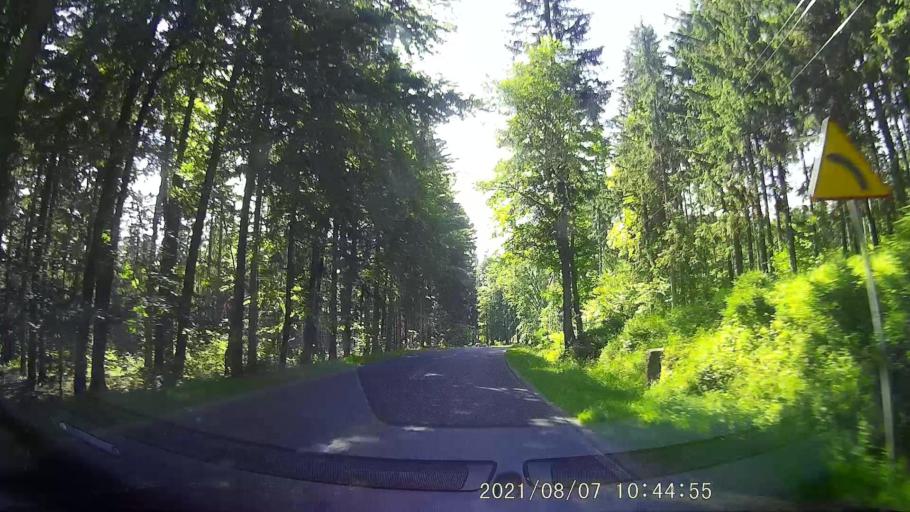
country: PL
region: Lower Silesian Voivodeship
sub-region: Powiat klodzki
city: Duszniki-Zdroj
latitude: 50.3269
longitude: 16.4116
